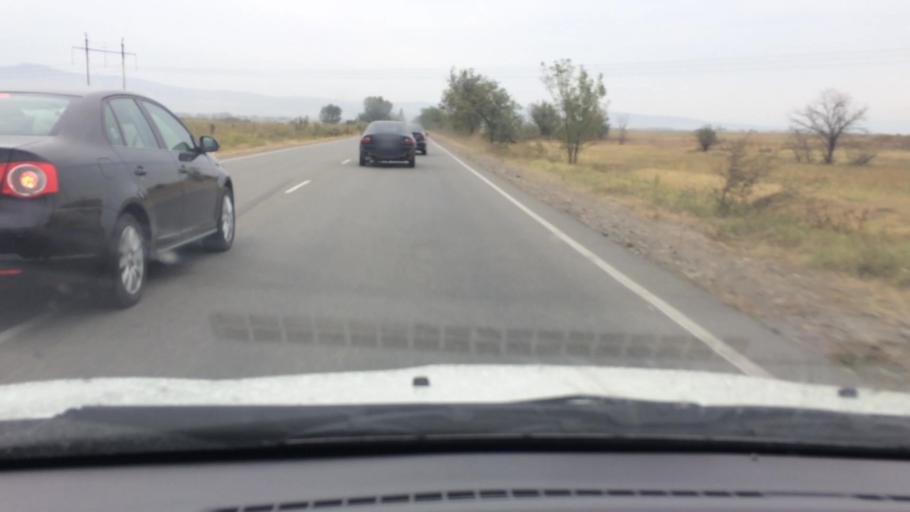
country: GE
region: Kvemo Kartli
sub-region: Marneuli
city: Marneuli
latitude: 41.5425
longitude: 44.7768
